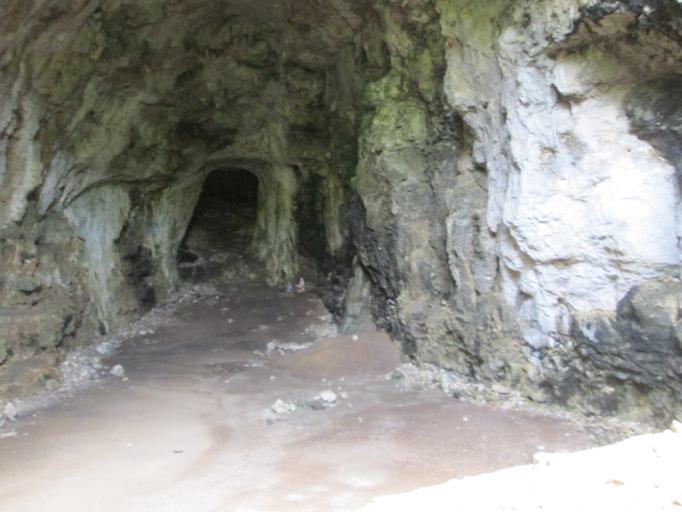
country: ES
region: Balearic Islands
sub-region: Illes Balears
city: Es Migjorn Gran
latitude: 39.9329
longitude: 4.0390
